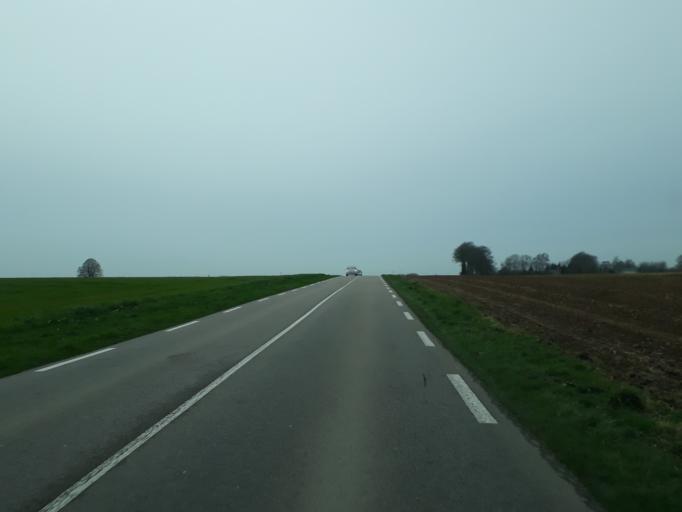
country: FR
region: Haute-Normandie
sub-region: Departement de la Seine-Maritime
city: Breaute
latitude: 49.6343
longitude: 0.3872
